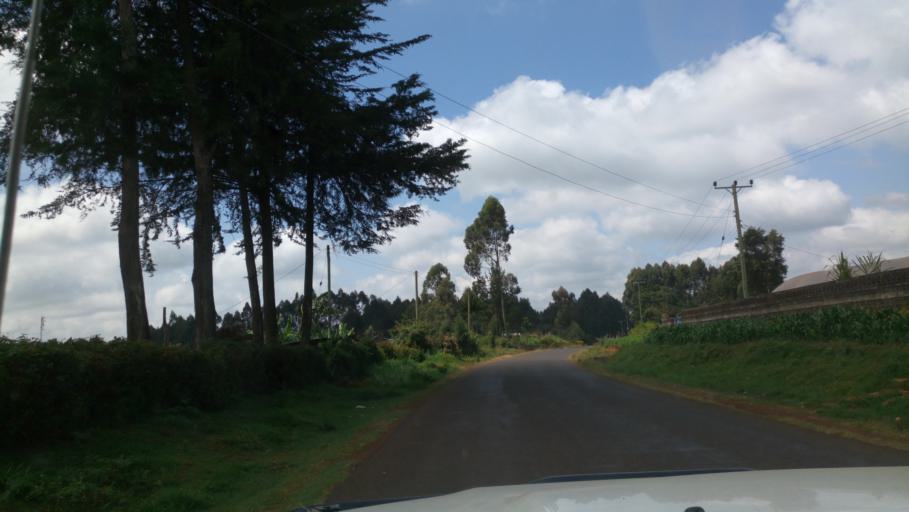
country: KE
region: Murang'a District
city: Kangema
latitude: -0.7714
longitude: 36.8404
